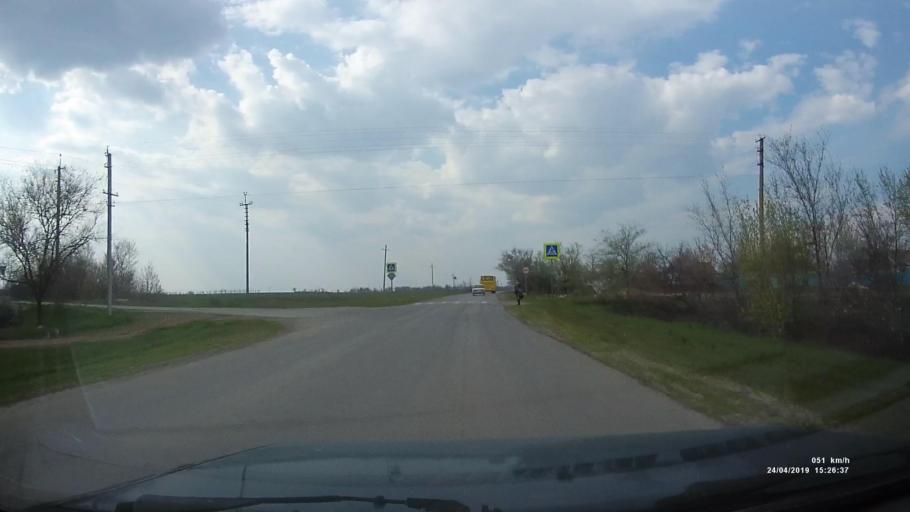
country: RU
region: Rostov
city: Remontnoye
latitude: 46.5590
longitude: 43.0309
